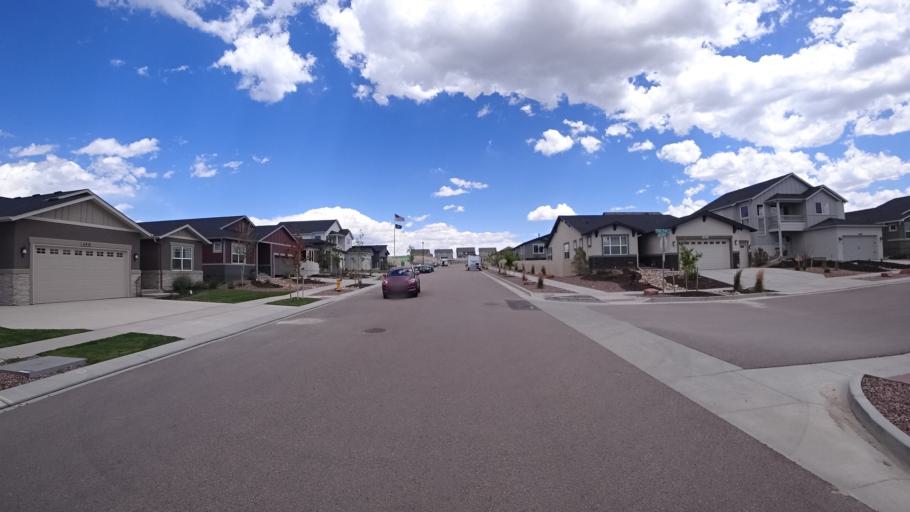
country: US
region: Colorado
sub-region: El Paso County
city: Black Forest
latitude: 38.9509
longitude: -104.7082
